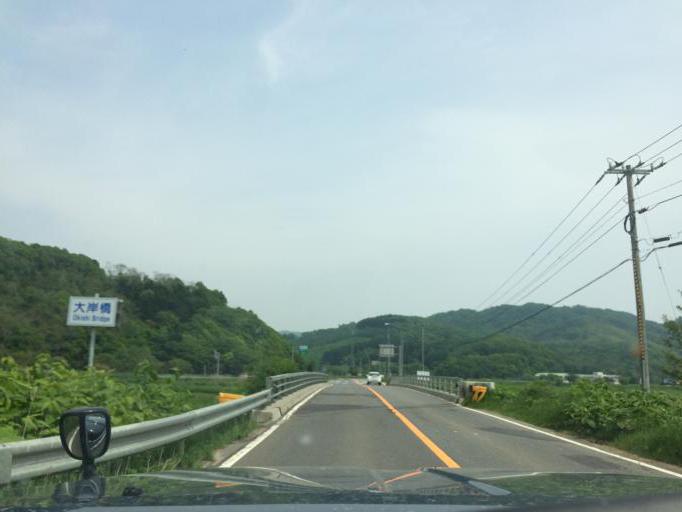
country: JP
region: Hokkaido
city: Niseko Town
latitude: 42.5988
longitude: 140.6374
